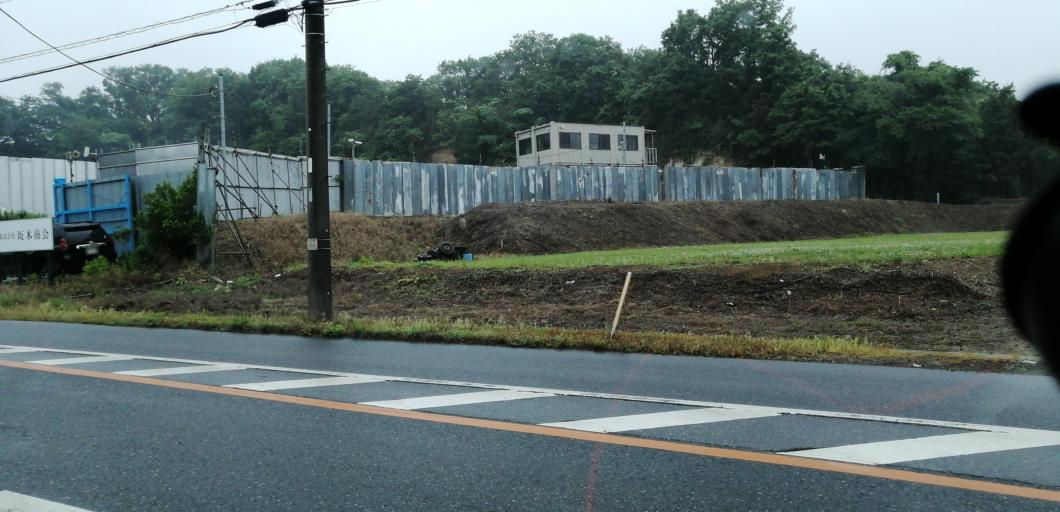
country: JP
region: Chiba
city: Ichihara
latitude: 35.4637
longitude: 140.1087
